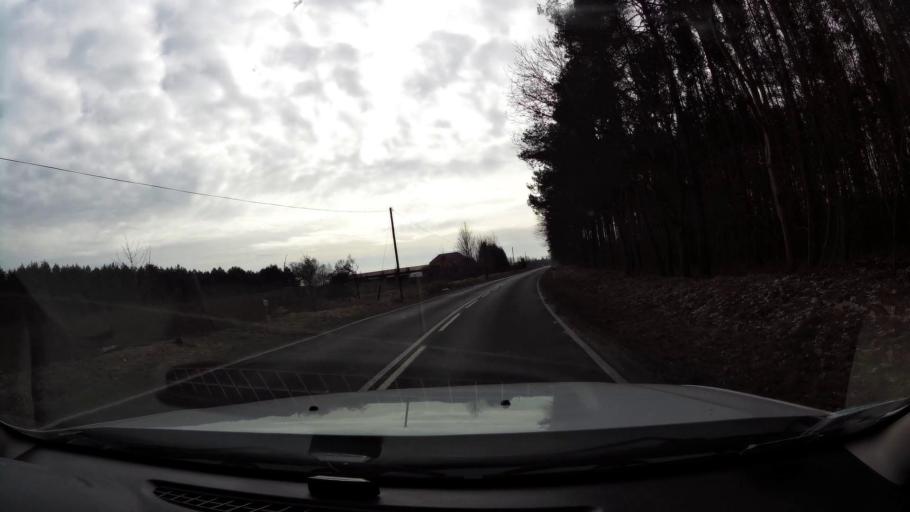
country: PL
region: West Pomeranian Voivodeship
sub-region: Powiat mysliborski
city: Debno
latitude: 52.7548
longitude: 14.6878
